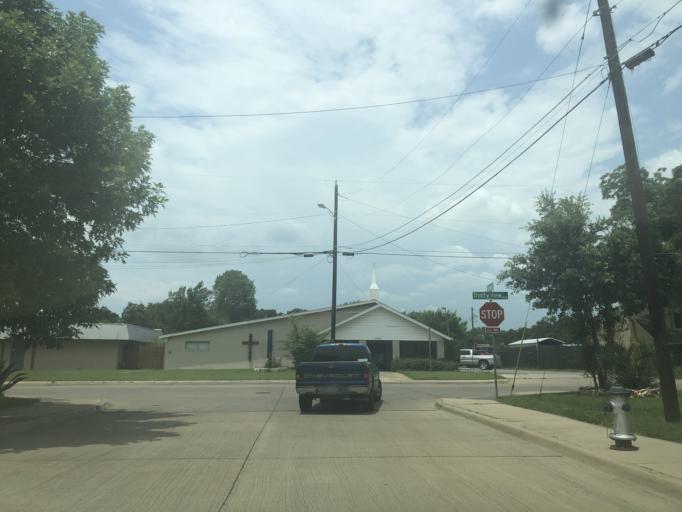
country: US
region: Texas
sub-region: Dallas County
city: Irving
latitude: 32.7991
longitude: -96.9322
